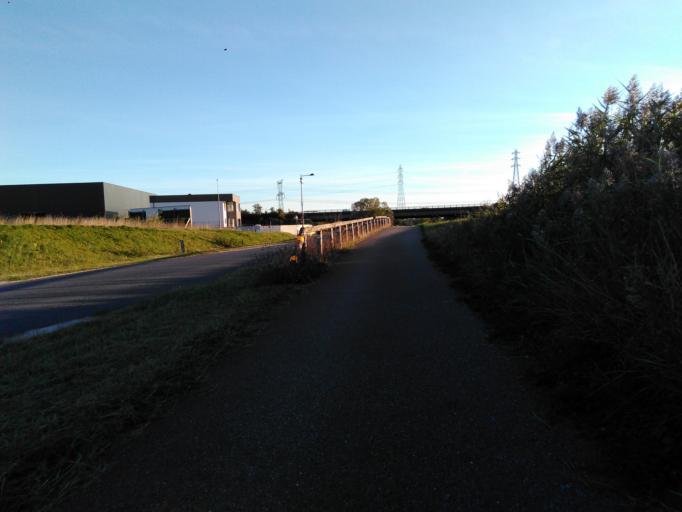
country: FR
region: Lorraine
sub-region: Departement de la Moselle
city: Maizieres-les-Metz
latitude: 49.2034
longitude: 6.1810
